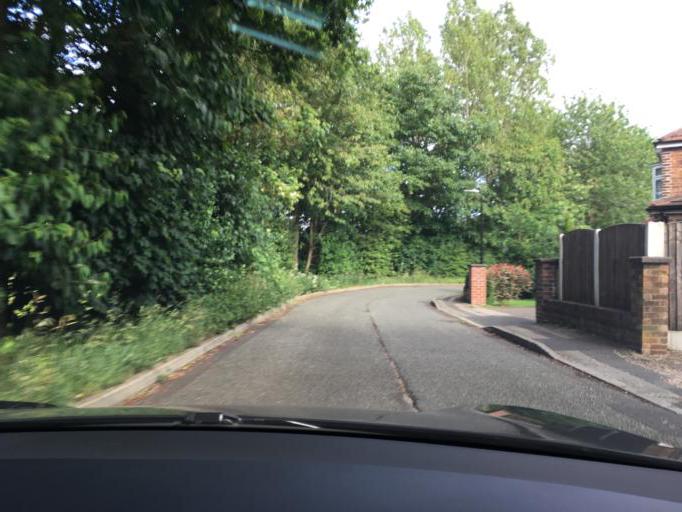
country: GB
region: England
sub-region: Trafford
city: Urmston
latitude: 53.4413
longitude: -2.3656
